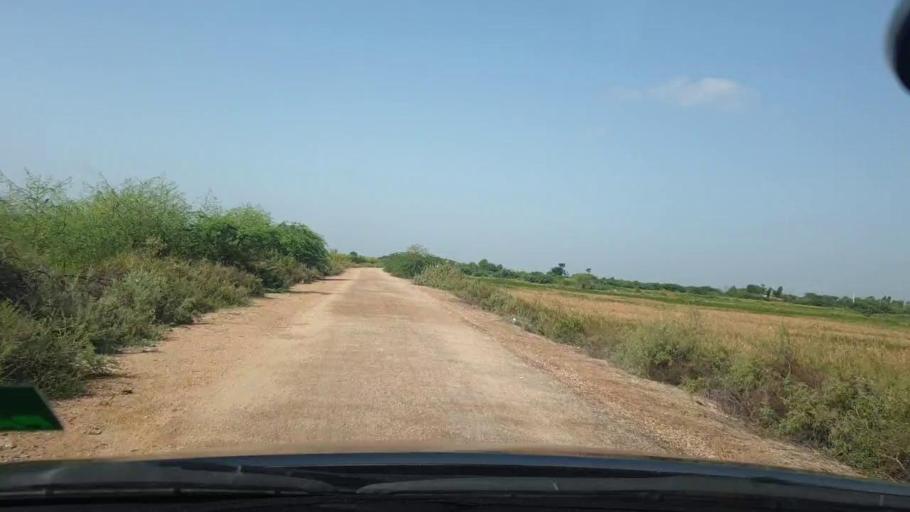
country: PK
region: Sindh
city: Tando Bago
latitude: 24.6854
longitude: 69.0141
